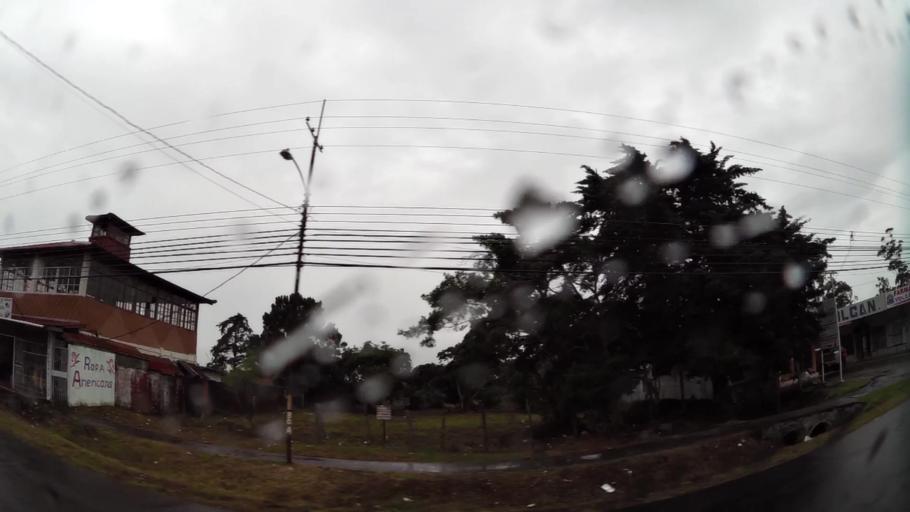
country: PA
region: Chiriqui
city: Volcan
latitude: 8.7811
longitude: -82.6462
